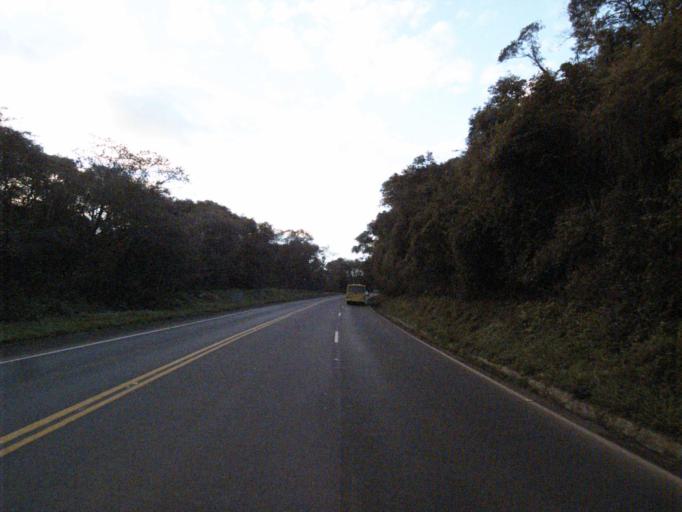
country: BR
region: Santa Catarina
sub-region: Joacaba
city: Joacaba
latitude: -27.2018
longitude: -51.5155
